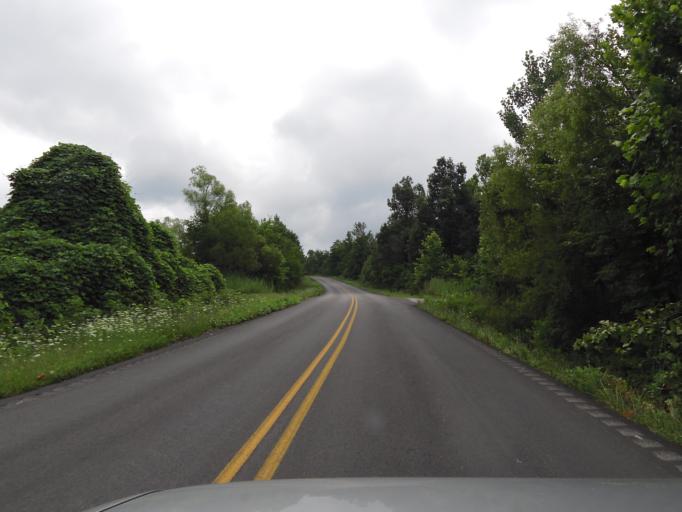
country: US
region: Kentucky
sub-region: Hopkins County
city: Madisonville
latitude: 37.3003
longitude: -87.3639
